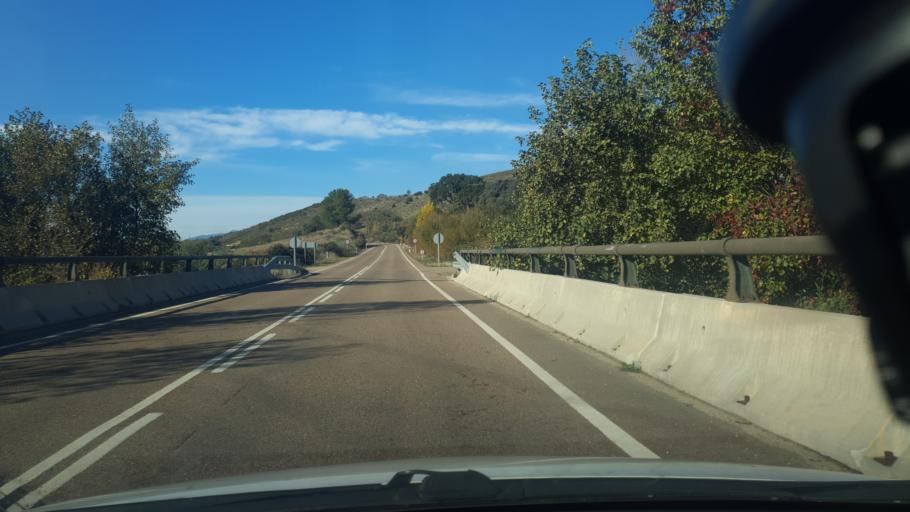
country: ES
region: Castille and Leon
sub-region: Provincia de Avila
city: Poyales del Hoyo
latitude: 40.1584
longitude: -5.1574
